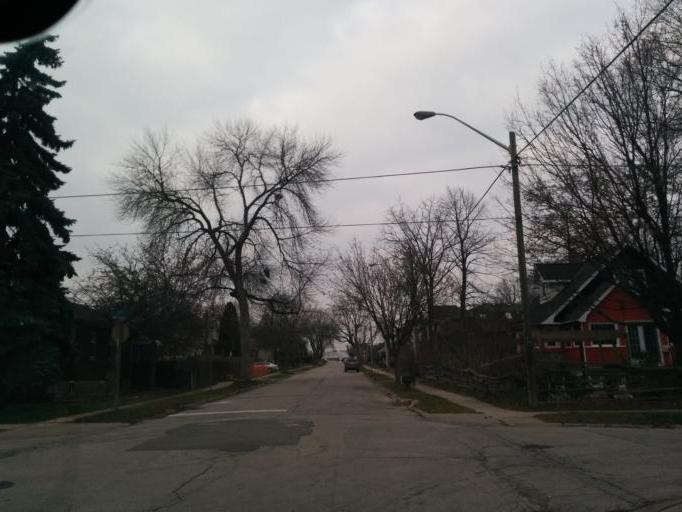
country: CA
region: Ontario
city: Etobicoke
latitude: 43.5908
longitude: -79.5384
